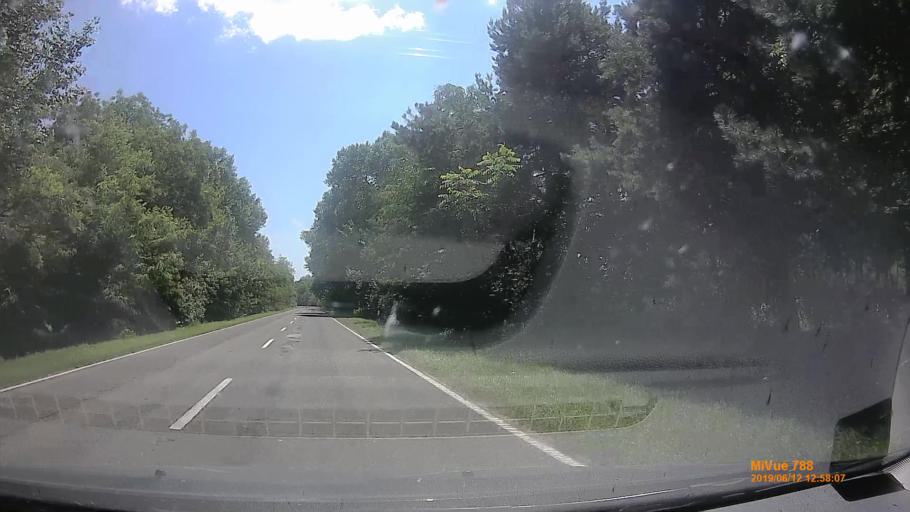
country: HU
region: Bacs-Kiskun
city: Palmonostora
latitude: 46.6263
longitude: 19.8971
